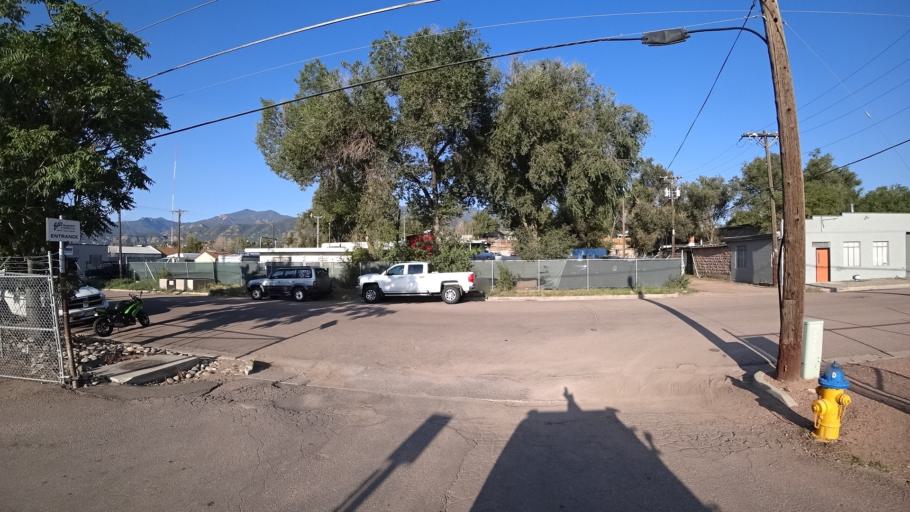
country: US
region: Colorado
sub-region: El Paso County
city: Colorado Springs
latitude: 38.8320
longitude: -104.8359
